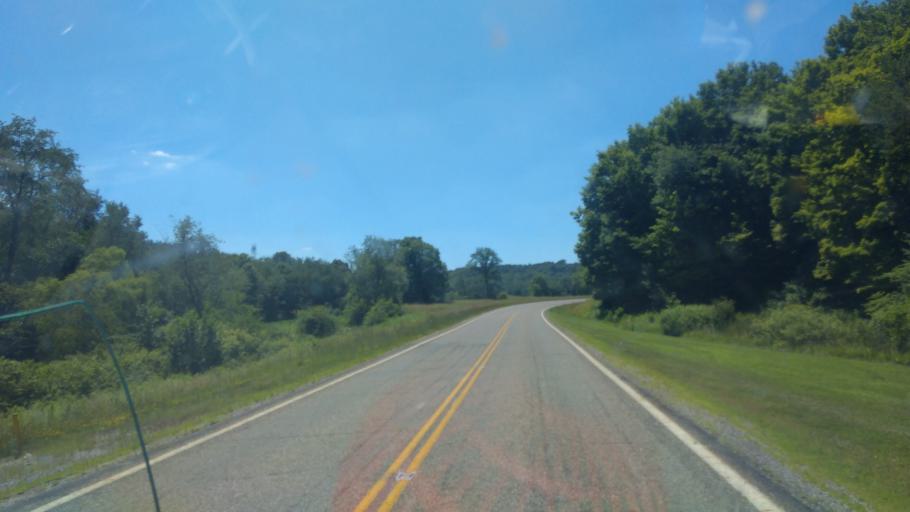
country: US
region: Ohio
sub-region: Columbiana County
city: Salineville
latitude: 40.6256
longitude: -80.8737
